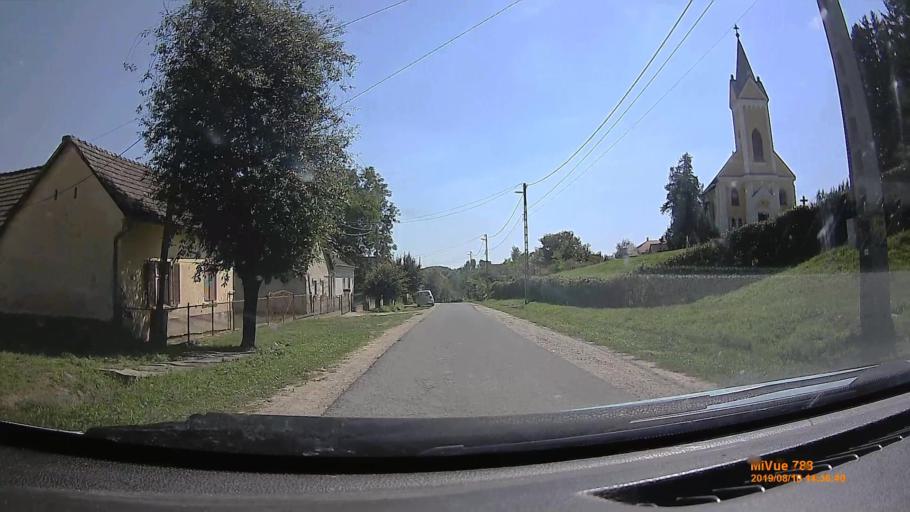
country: HU
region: Somogy
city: Somogyvar
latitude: 46.5690
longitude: 17.6839
